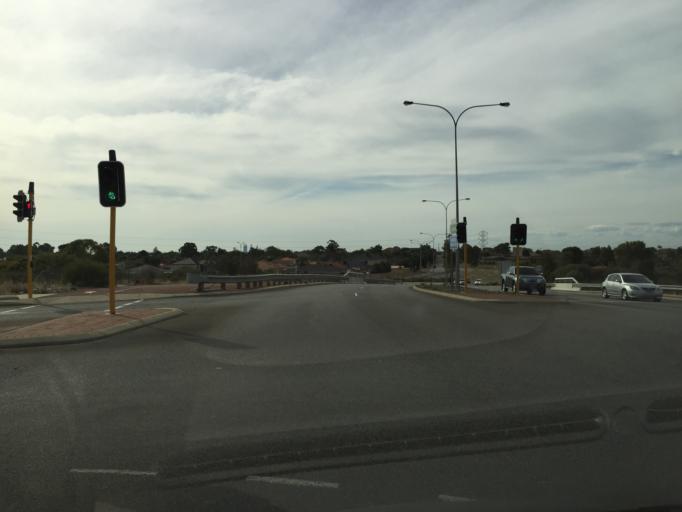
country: AU
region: Western Australia
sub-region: Canning
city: Canning Vale
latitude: -32.0567
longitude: 115.9046
